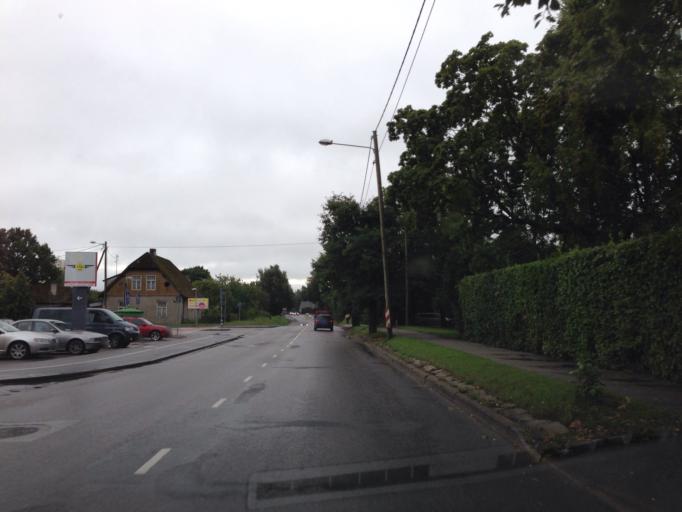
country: EE
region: Tartu
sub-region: Tartu linn
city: Tartu
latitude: 58.3617
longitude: 26.7212
